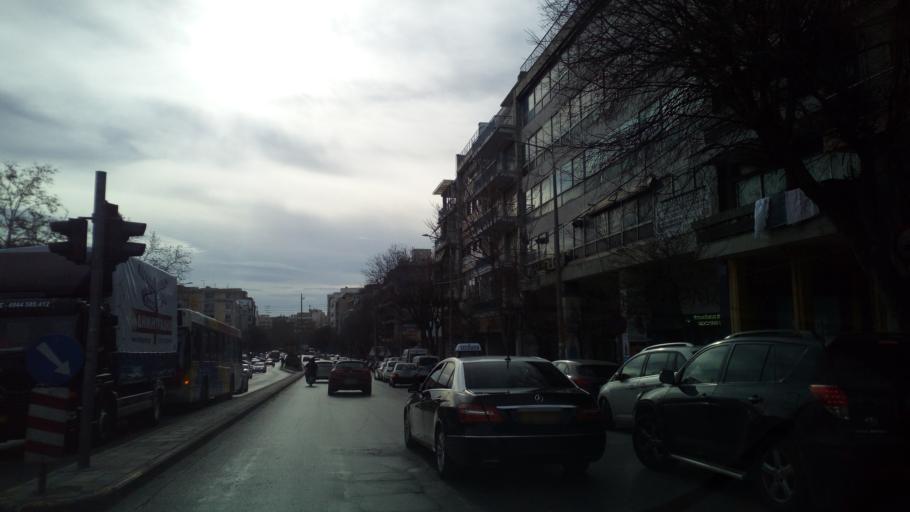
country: GR
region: Central Macedonia
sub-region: Nomos Thessalonikis
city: Thessaloniki
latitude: 40.6447
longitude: 22.9352
